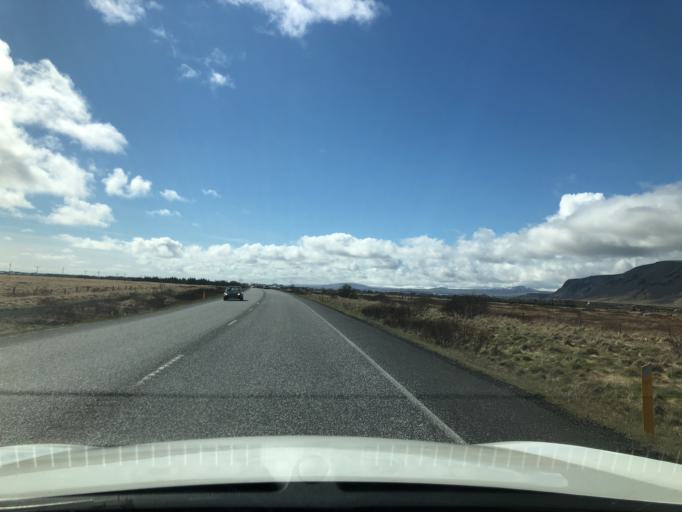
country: IS
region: South
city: Selfoss
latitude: 63.9414
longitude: -20.9390
